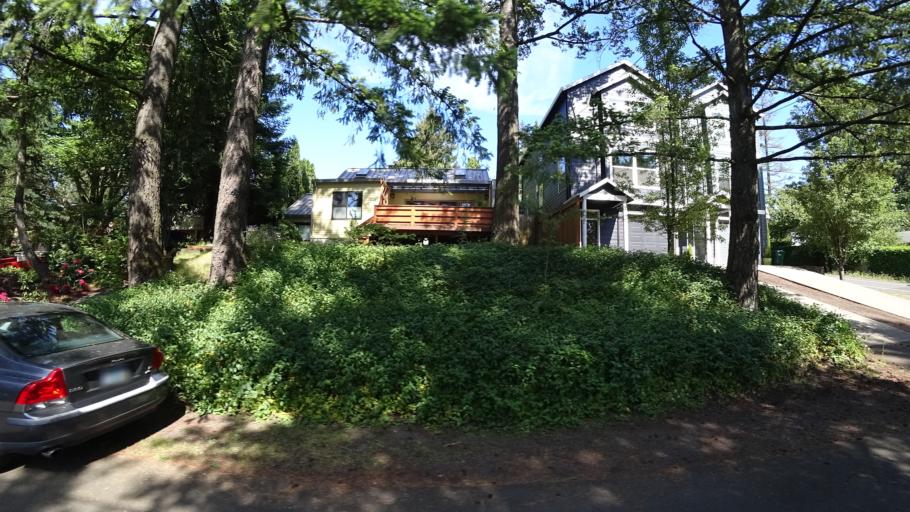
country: US
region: Oregon
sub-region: Washington County
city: Metzger
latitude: 45.4457
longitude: -122.7291
